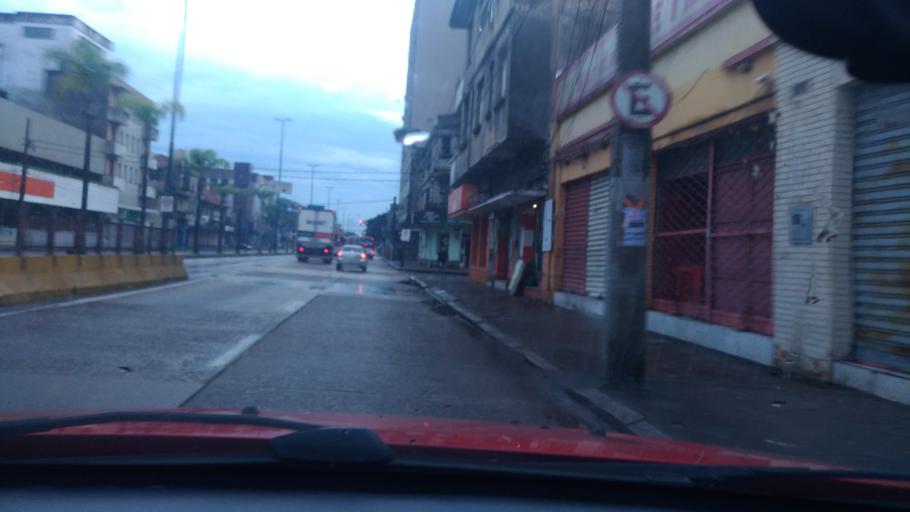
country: BR
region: Rio Grande do Sul
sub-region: Porto Alegre
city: Porto Alegre
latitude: -30.0116
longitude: -51.2030
